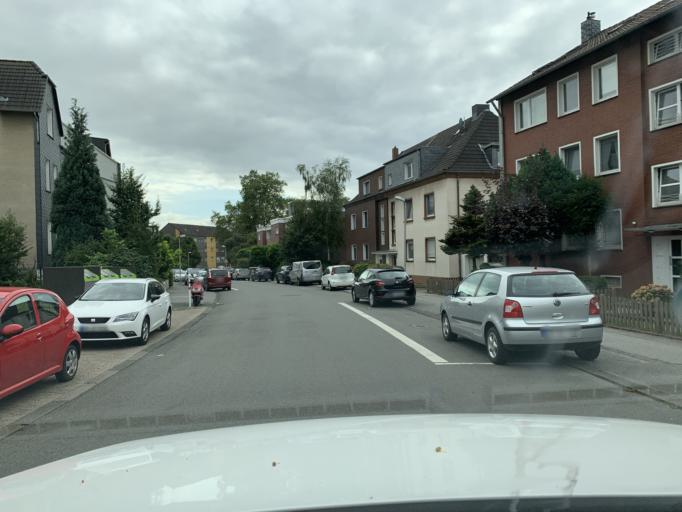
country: DE
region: North Rhine-Westphalia
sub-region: Regierungsbezirk Dusseldorf
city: Muelheim (Ruhr)
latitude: 51.4436
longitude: 6.8998
